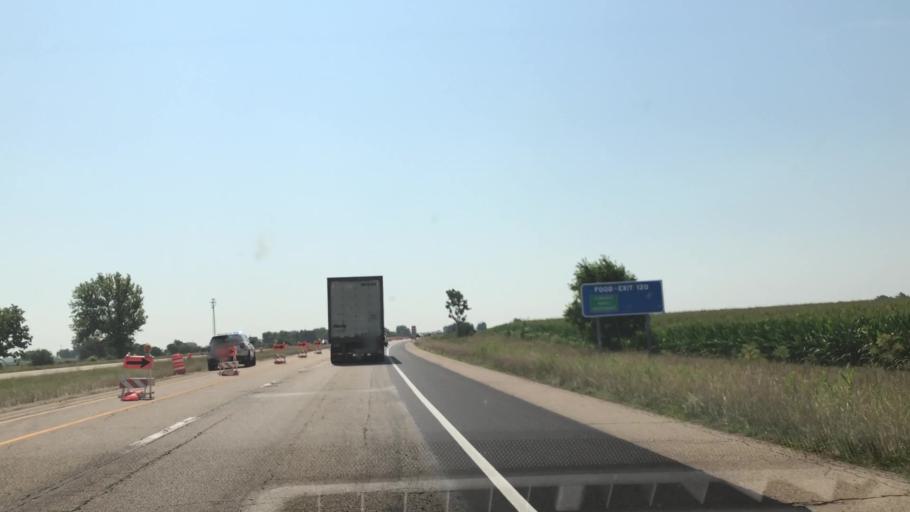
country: US
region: Illinois
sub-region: McLean County
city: Danvers
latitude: 40.5999
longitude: -89.1659
